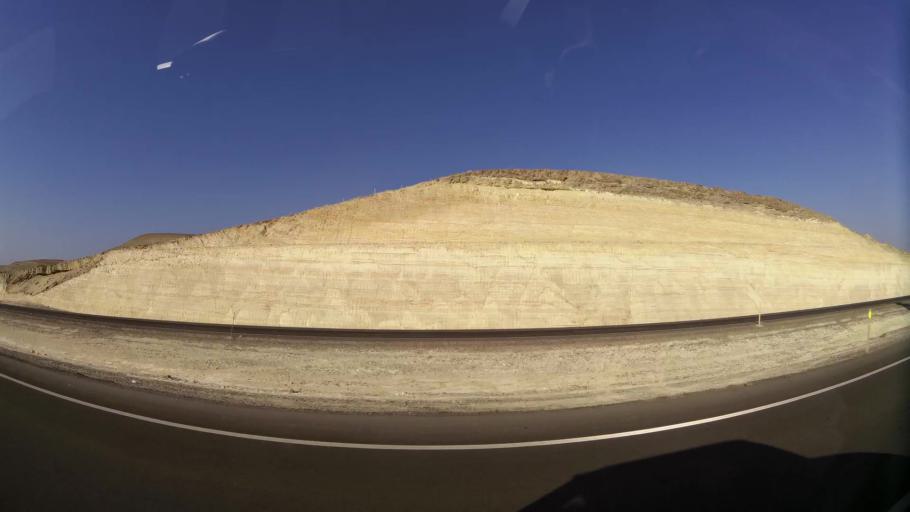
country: PE
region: Ica
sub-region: Provincia de Pisco
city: San Clemente
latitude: -13.6597
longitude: -76.1739
